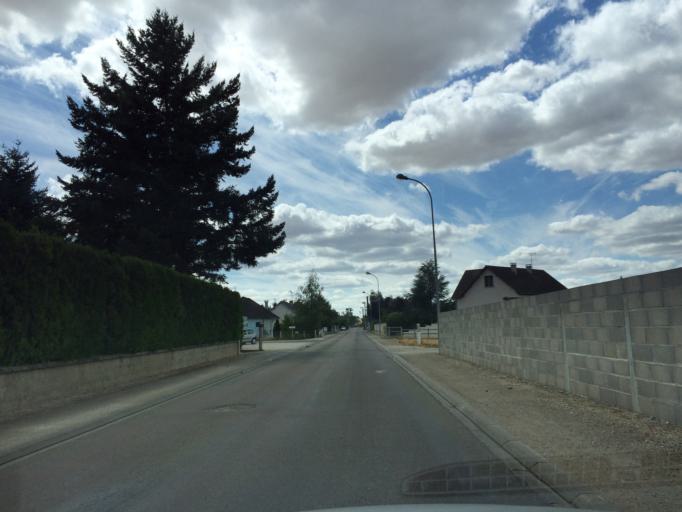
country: FR
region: Bourgogne
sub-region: Departement de l'Yonne
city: Laroche-Saint-Cydroine
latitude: 47.9518
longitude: 3.4838
